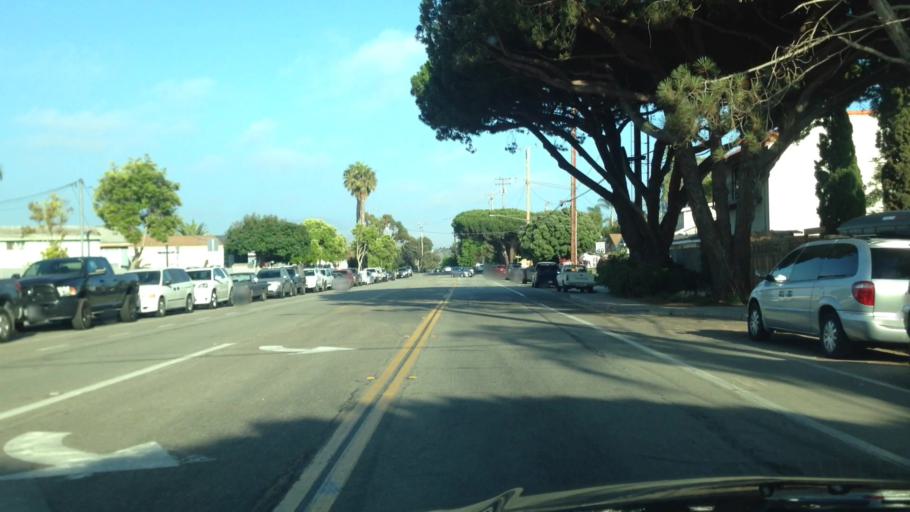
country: US
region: California
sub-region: Santa Barbara County
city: Carpinteria
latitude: 34.4030
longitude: -119.5313
